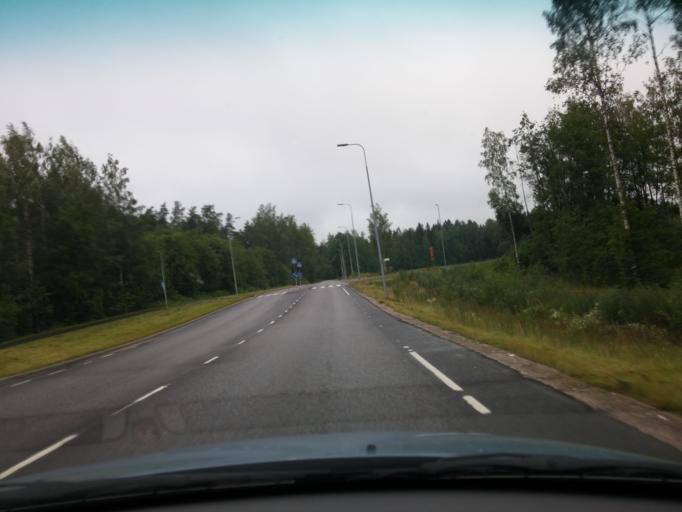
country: FI
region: Uusimaa
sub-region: Helsinki
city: Kauniainen
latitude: 60.3241
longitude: 24.7150
